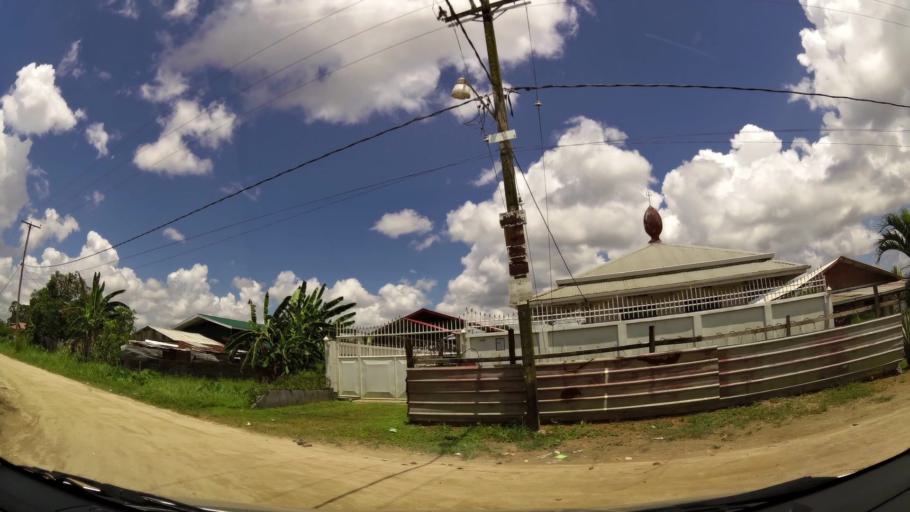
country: SR
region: Paramaribo
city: Paramaribo
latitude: 5.8536
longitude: -55.1721
